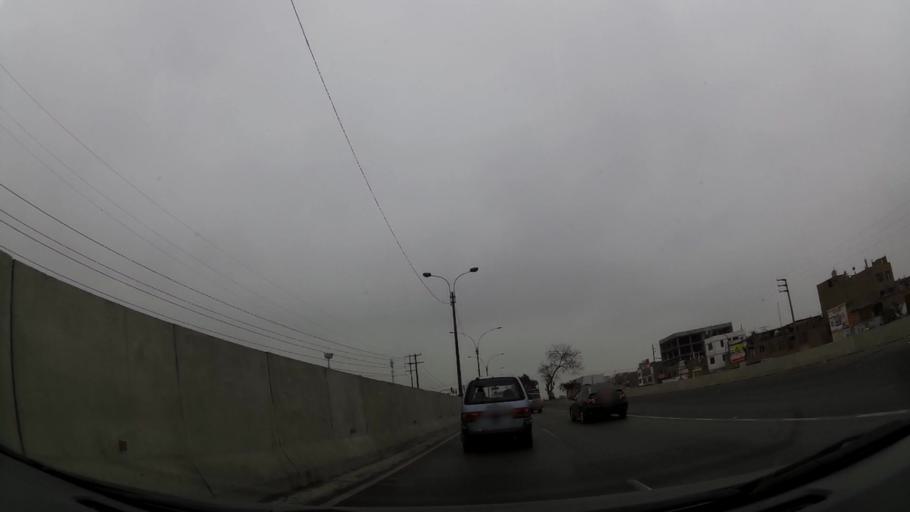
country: PE
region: Lima
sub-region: Lima
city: Urb. Santo Domingo
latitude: -11.9240
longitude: -77.0731
